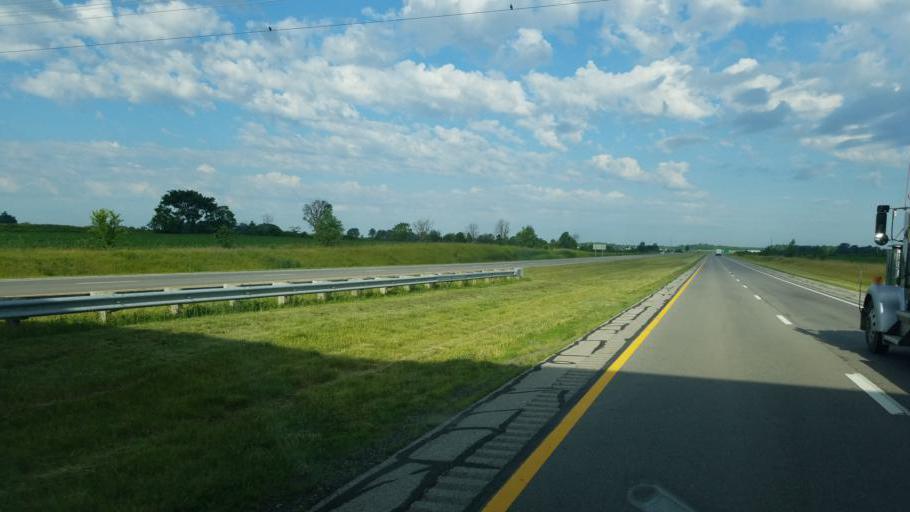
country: US
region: Ohio
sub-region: Crawford County
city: Galion
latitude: 40.7622
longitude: -82.8197
